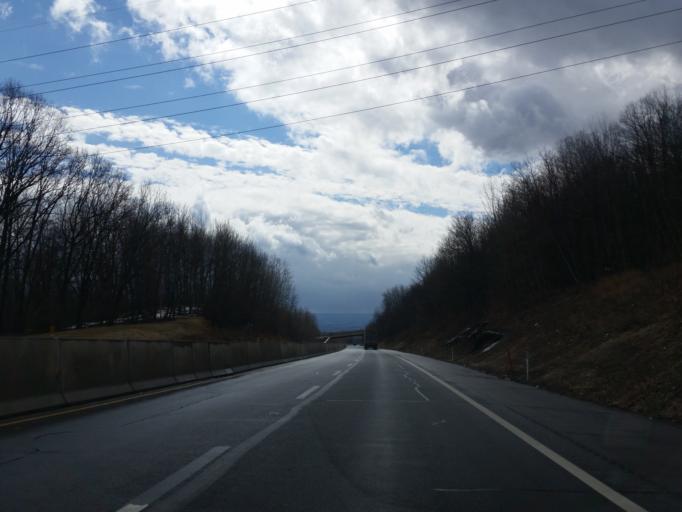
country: US
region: Pennsylvania
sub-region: Lackawanna County
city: Taylor
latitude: 41.4154
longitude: -75.7184
